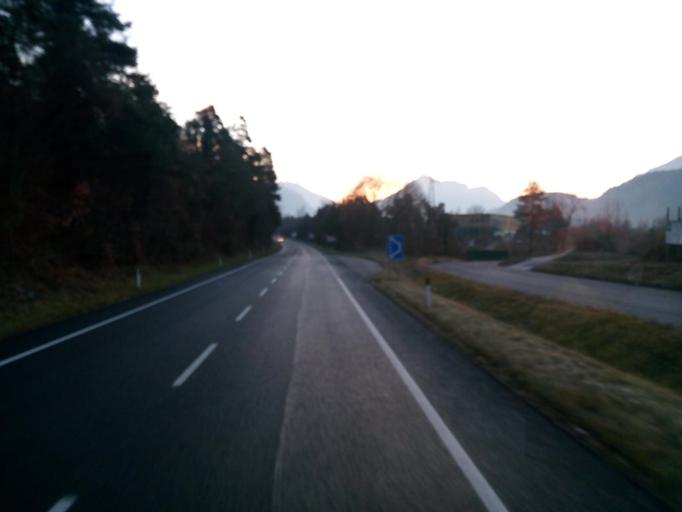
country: IT
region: Friuli Venezia Giulia
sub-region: Provincia di Udine
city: Chiaulis
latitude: 46.4088
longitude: 12.9710
